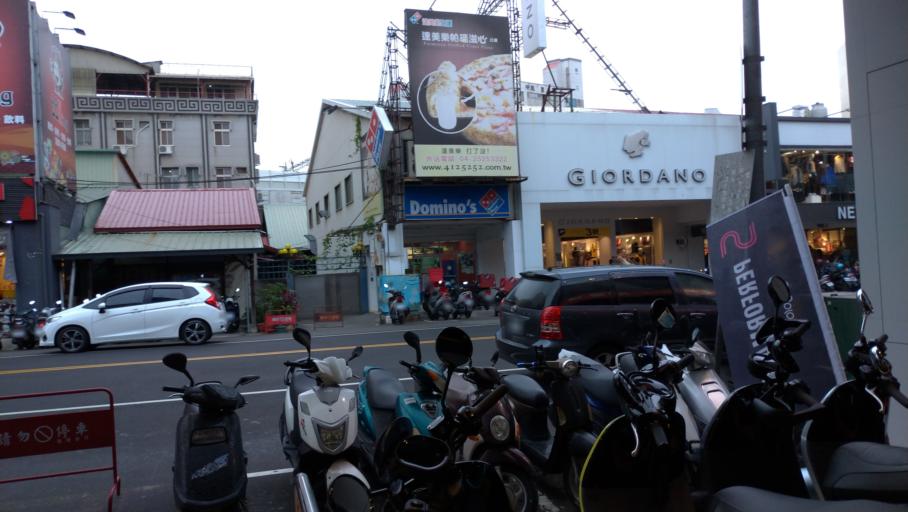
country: TW
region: Taiwan
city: Fengyuan
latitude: 24.2531
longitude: 120.7221
